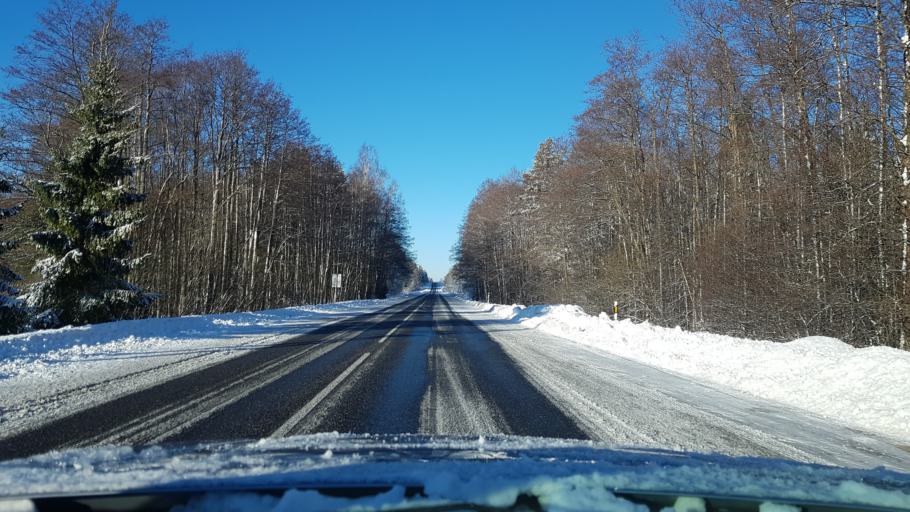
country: EE
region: Hiiumaa
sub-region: Kaerdla linn
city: Kardla
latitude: 58.9563
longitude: 22.8642
